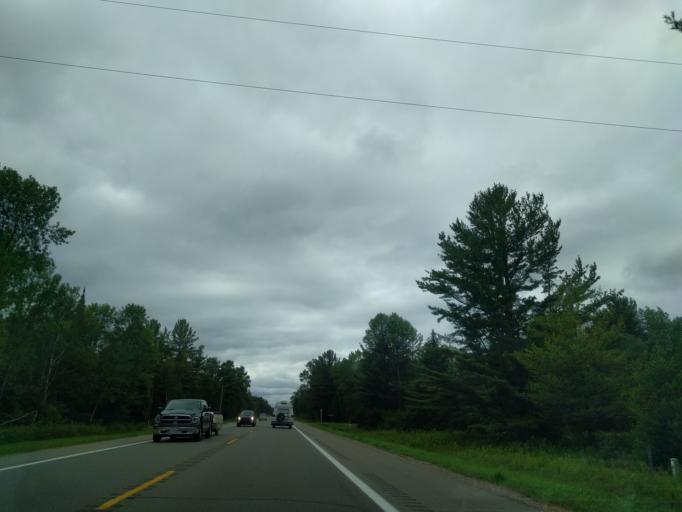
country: US
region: Michigan
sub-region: Menominee County
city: Menominee
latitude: 45.3173
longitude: -87.4331
